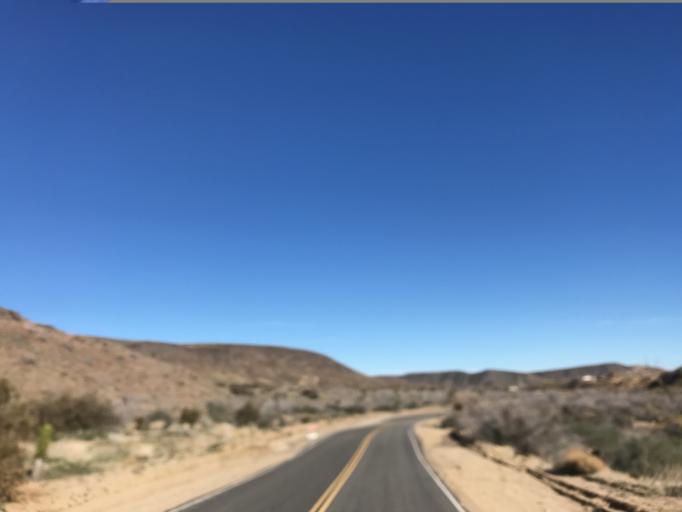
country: US
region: California
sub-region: San Bernardino County
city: Yucca Valley
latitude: 34.1620
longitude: -116.5098
